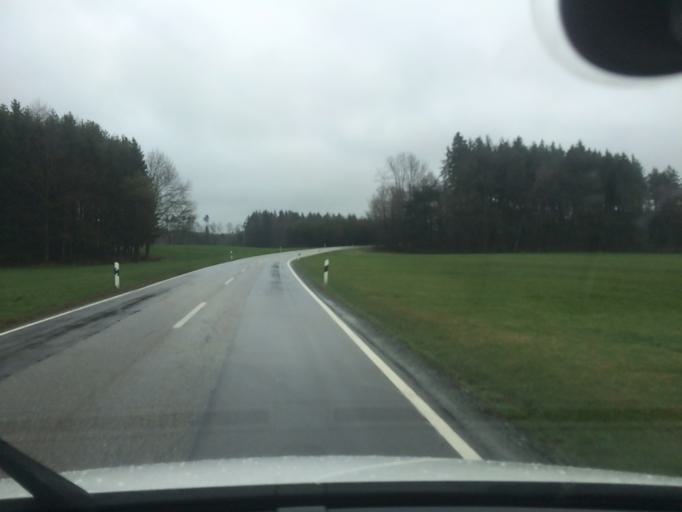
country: DE
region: Bavaria
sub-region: Upper Bavaria
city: Tuntenhausen
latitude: 47.9469
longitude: 11.9743
